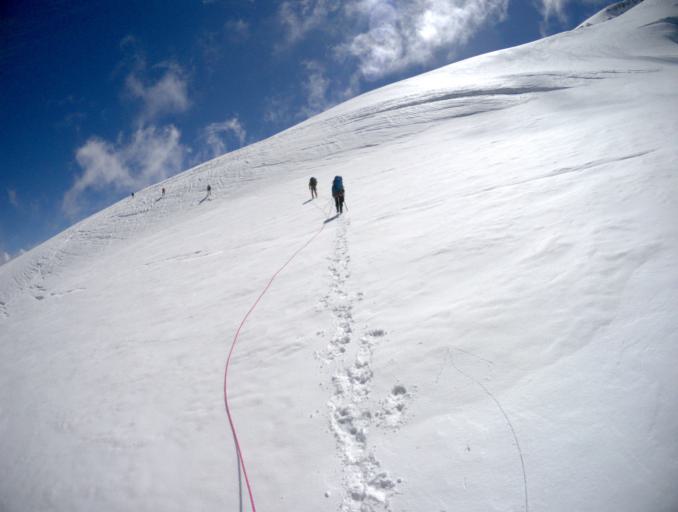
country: RU
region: Kabardino-Balkariya
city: Terskol
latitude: 43.3815
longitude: 42.4401
